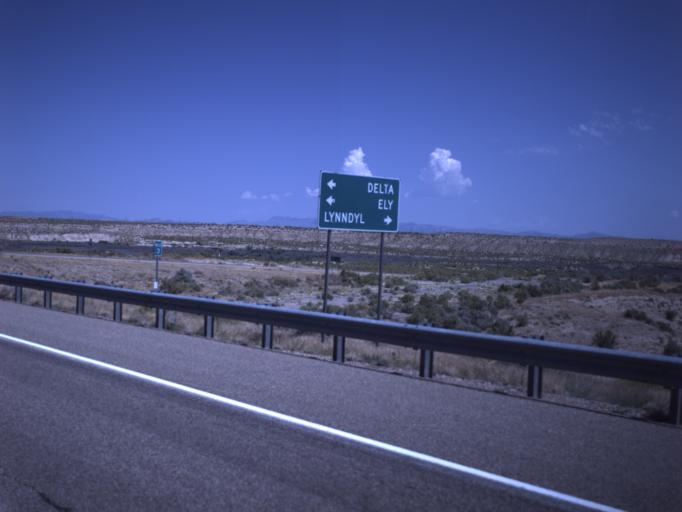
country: US
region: Utah
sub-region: Millard County
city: Delta
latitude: 39.3957
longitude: -112.5028
